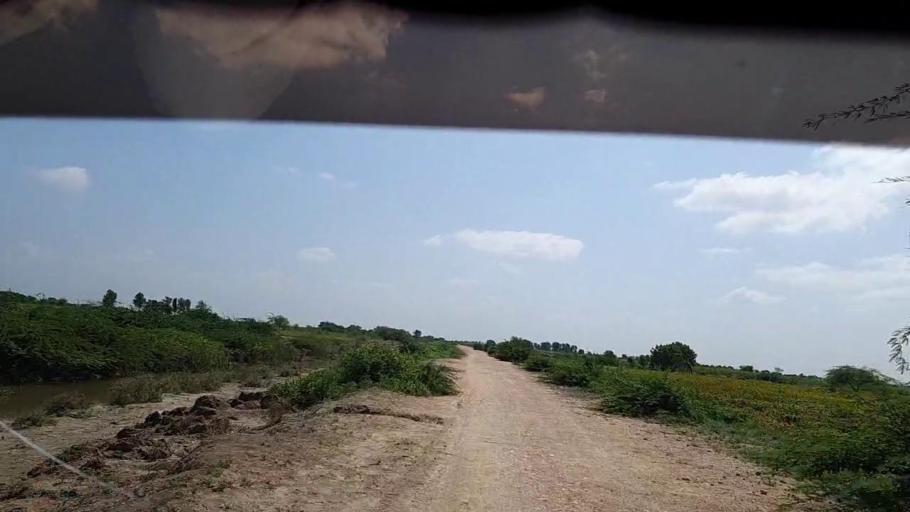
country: PK
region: Sindh
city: Kadhan
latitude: 24.5962
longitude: 68.9917
